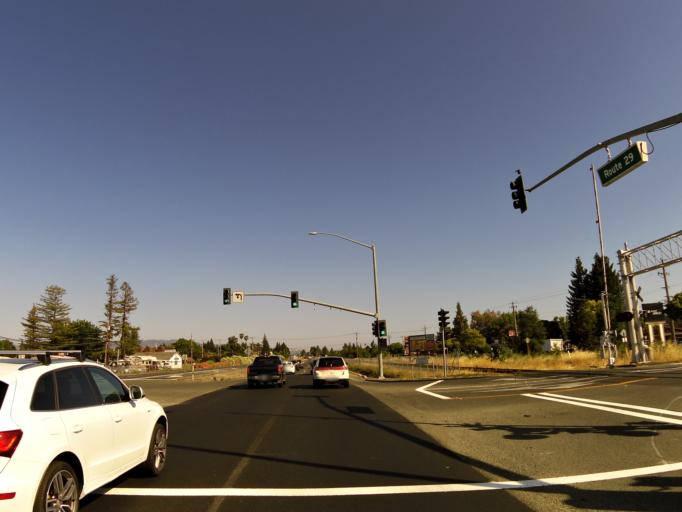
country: US
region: California
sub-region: Napa County
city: Napa
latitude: 38.3364
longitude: -122.3220
